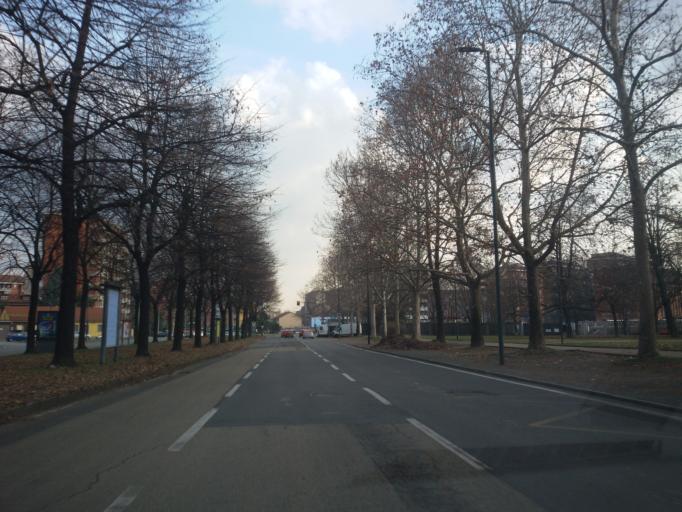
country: IT
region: Piedmont
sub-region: Provincia di Torino
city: Lesna
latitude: 45.0437
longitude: 7.6276
